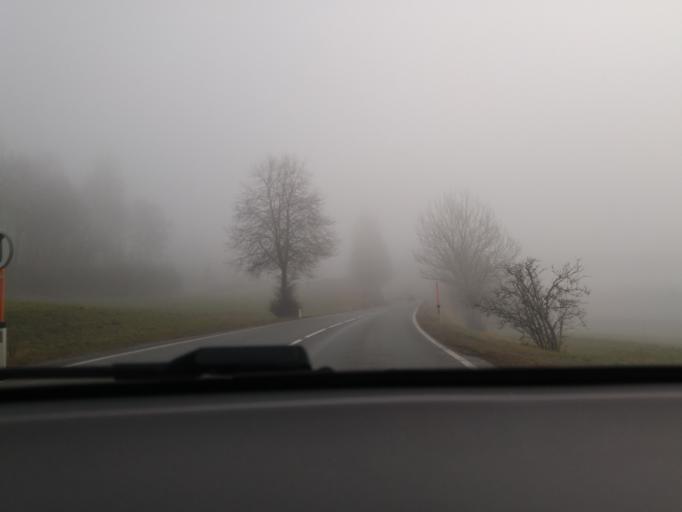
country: AT
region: Salzburg
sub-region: Politischer Bezirk Zell am See
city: Bruck an der Grossglocknerstrasse
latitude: 47.2855
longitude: 12.8499
